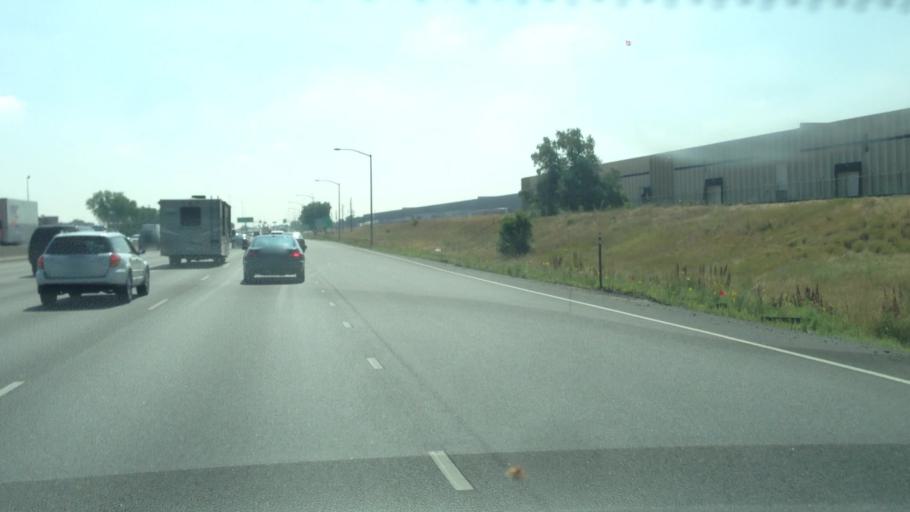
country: US
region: Colorado
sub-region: Adams County
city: Aurora
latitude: 39.7768
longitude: -104.8589
